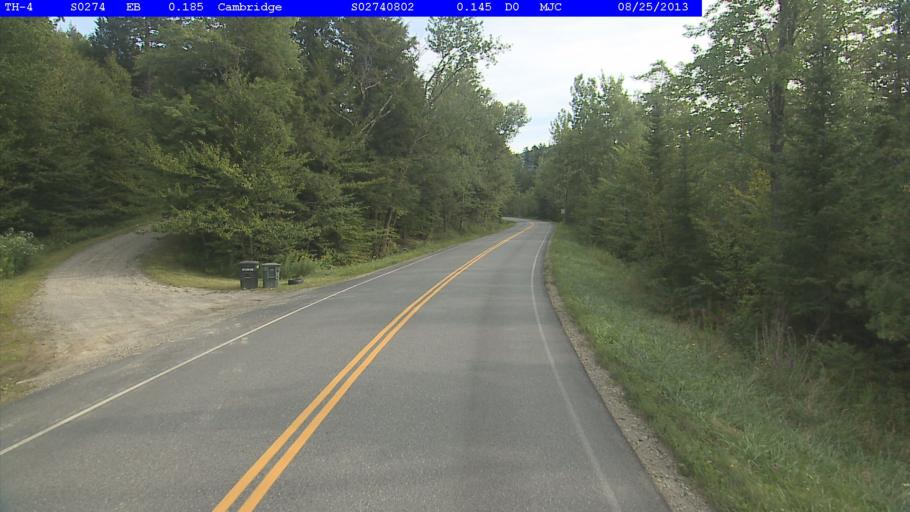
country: US
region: Vermont
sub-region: Lamoille County
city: Johnson
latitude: 44.6805
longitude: -72.7709
